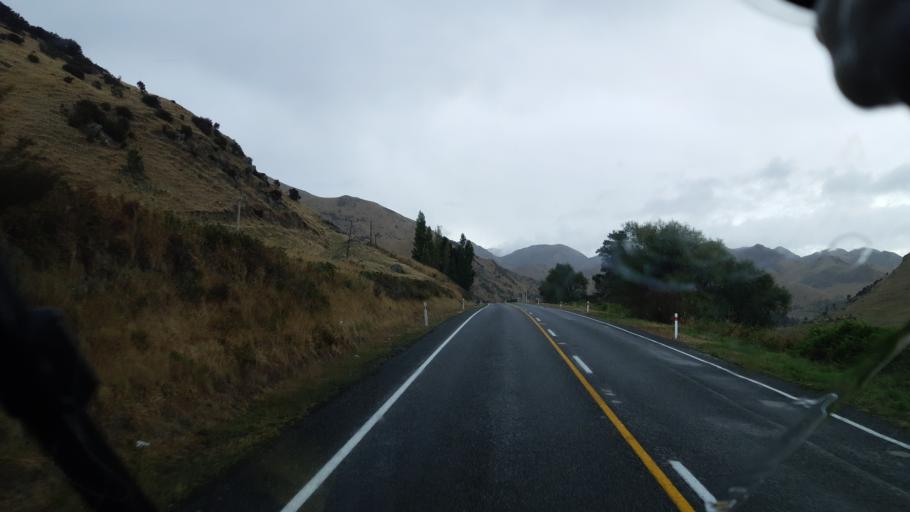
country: NZ
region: Canterbury
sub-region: Hurunui District
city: Amberley
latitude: -42.6718
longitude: 172.7739
